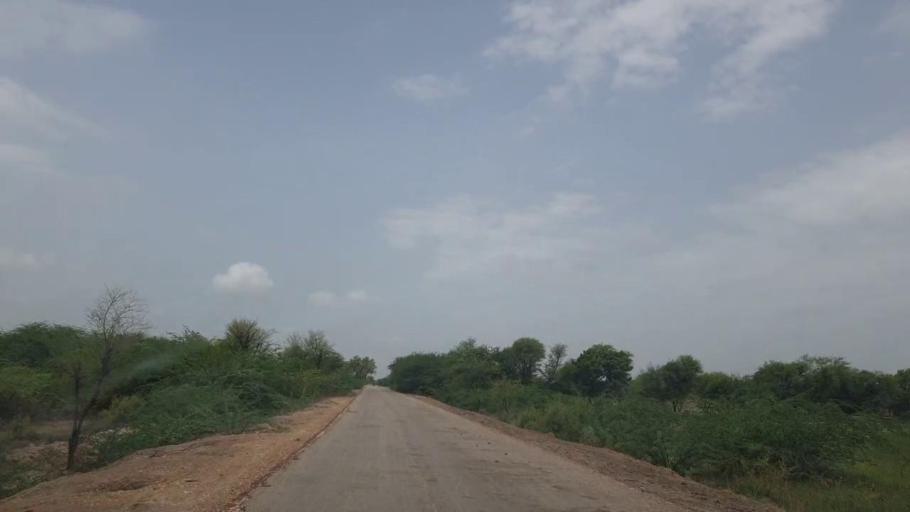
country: PK
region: Sindh
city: Digri
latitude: 24.9391
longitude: 69.1571
